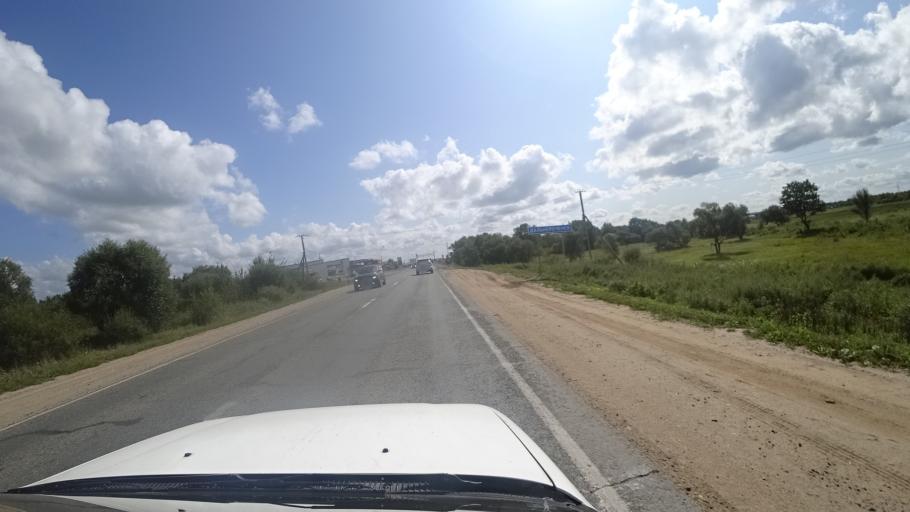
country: RU
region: Primorskiy
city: Dal'nerechensk
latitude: 45.9215
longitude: 133.7730
